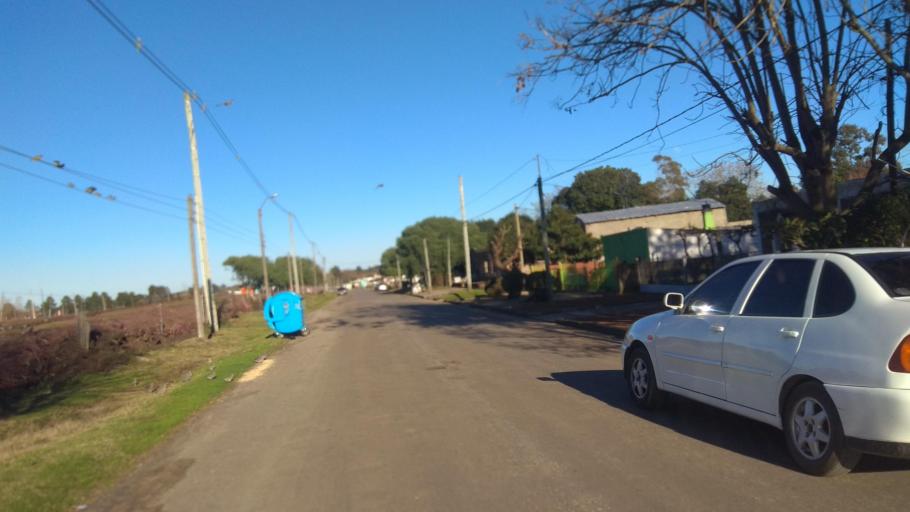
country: UY
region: Florida
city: Florida
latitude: -34.1005
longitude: -56.2380
